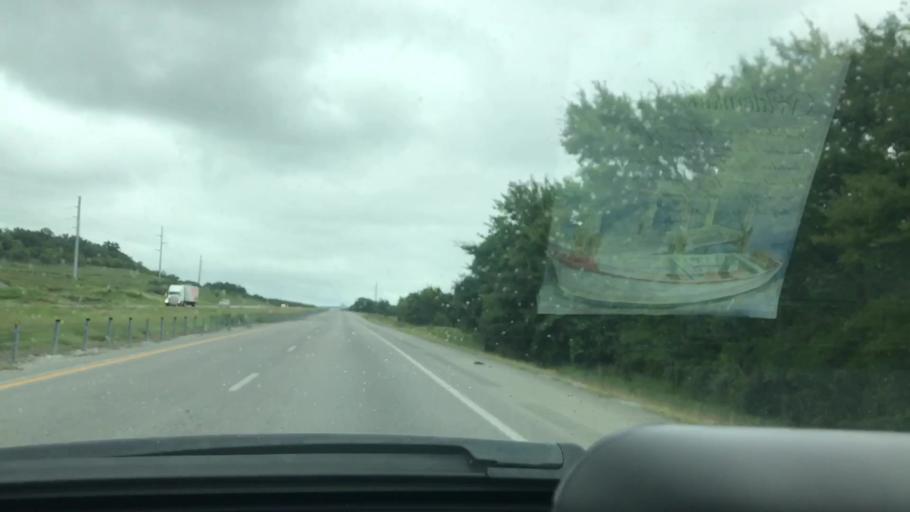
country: US
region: Oklahoma
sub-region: Coal County
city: Coalgate
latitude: 34.6494
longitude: -95.9430
